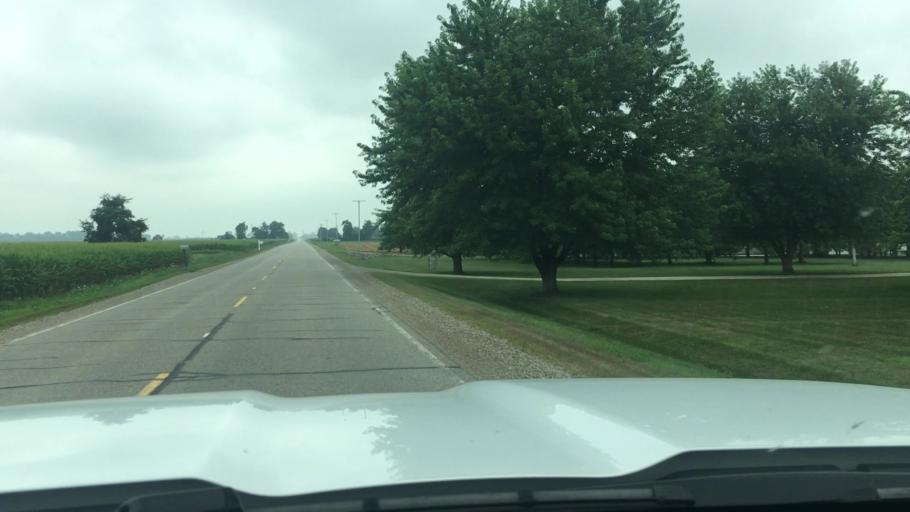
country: US
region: Michigan
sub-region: Sanilac County
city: Marlette
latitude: 43.2554
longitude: -83.0565
